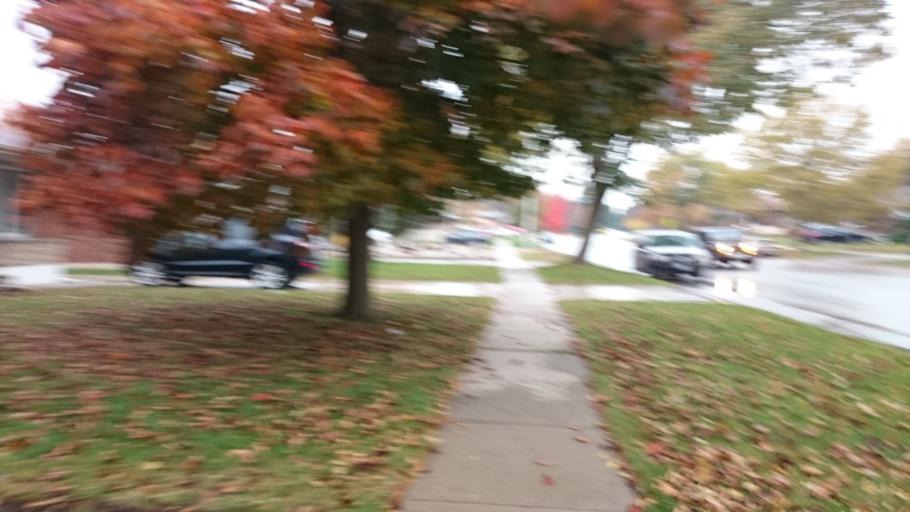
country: CA
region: Ontario
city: Brantford
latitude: 43.1703
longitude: -80.2895
